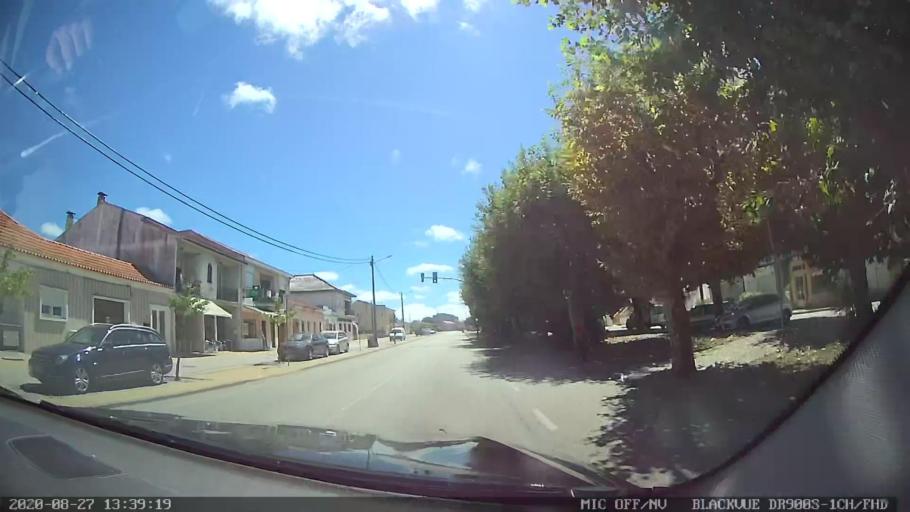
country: PT
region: Coimbra
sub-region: Mira
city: Mira
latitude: 40.4421
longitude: -8.7288
